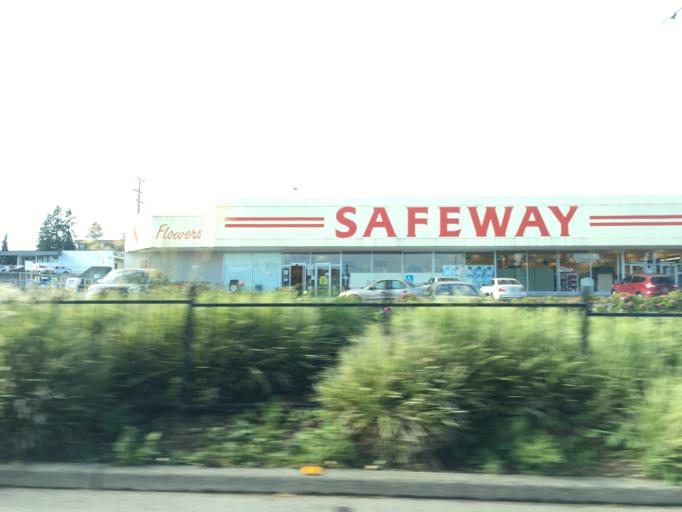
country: CA
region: British Columbia
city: Port Moody
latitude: 49.2490
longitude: -122.8645
